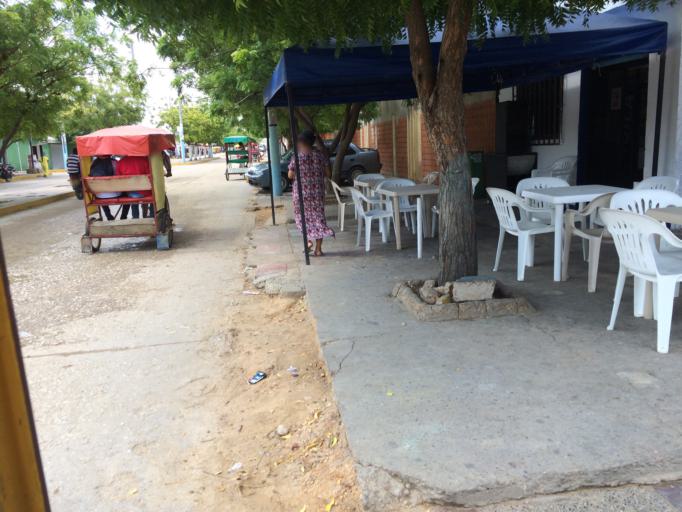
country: CO
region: La Guajira
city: Manaure
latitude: 11.7775
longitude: -72.4465
